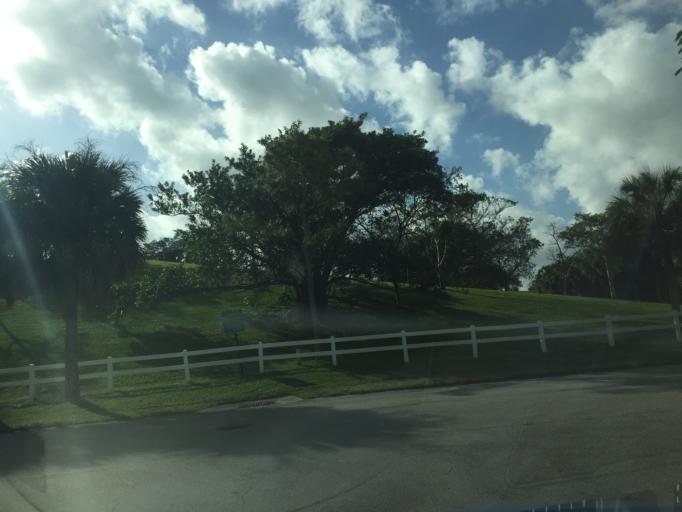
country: US
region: Florida
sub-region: Broward County
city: Tamarac
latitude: 26.2323
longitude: -80.2480
